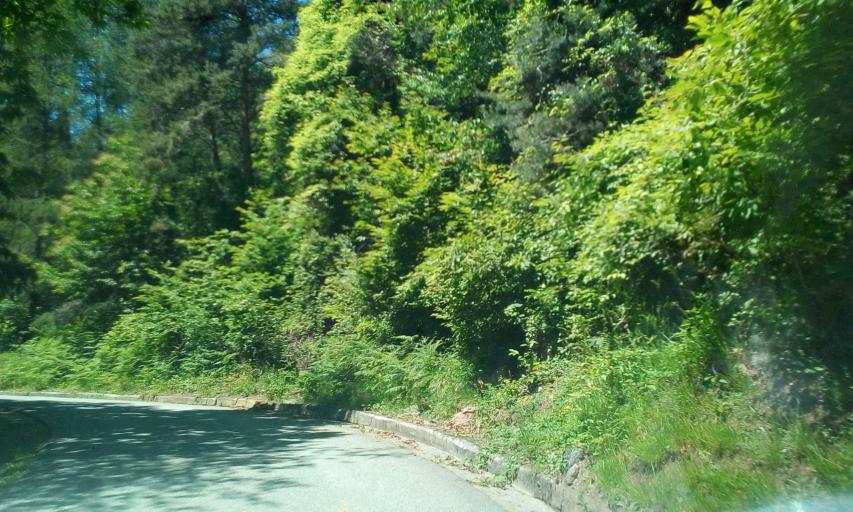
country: IT
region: Aosta Valley
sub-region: Valle d'Aosta
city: Challand-Saint-Victor
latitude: 45.7012
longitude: 7.7059
